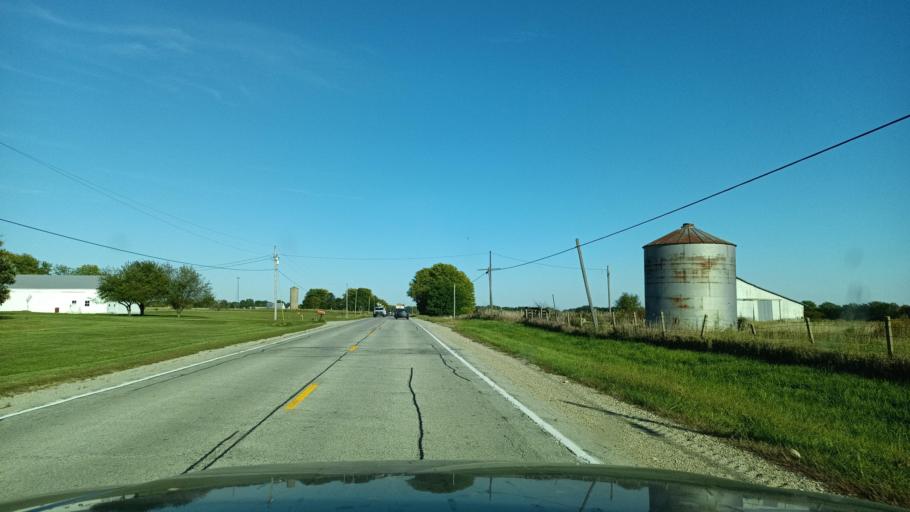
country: US
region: Illinois
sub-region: De Witt County
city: Farmer City
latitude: 40.2320
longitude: -88.6731
